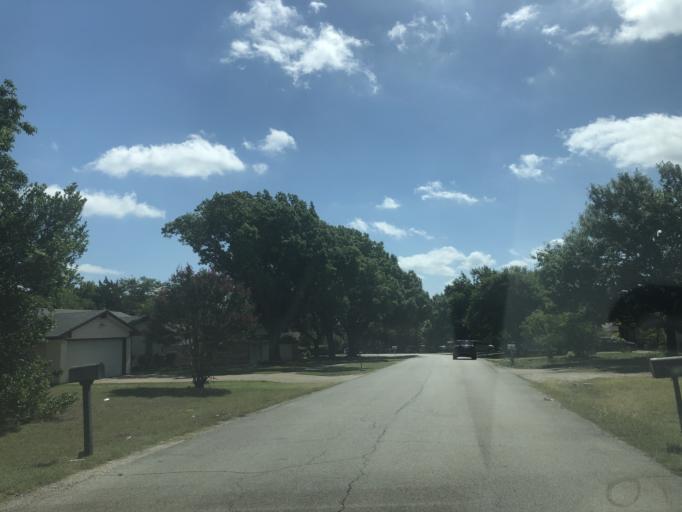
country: US
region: Texas
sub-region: Dallas County
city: Duncanville
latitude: 32.6589
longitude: -96.9244
